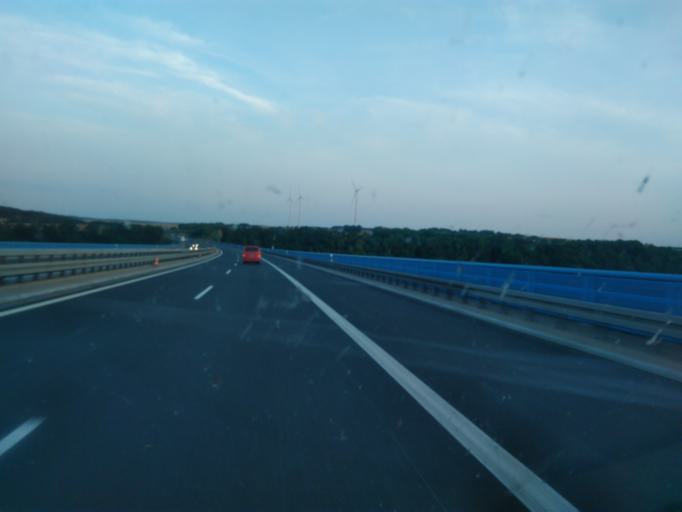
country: DE
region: Bavaria
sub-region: Regierungsbezirk Unterfranken
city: Munnerstadt
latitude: 50.2498
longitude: 10.2147
